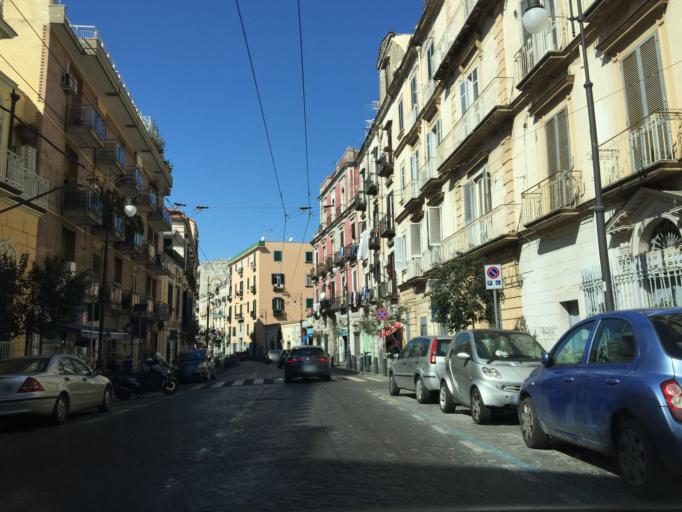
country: IT
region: Campania
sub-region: Provincia di Napoli
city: Portici
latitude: 40.8206
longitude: 14.3273
